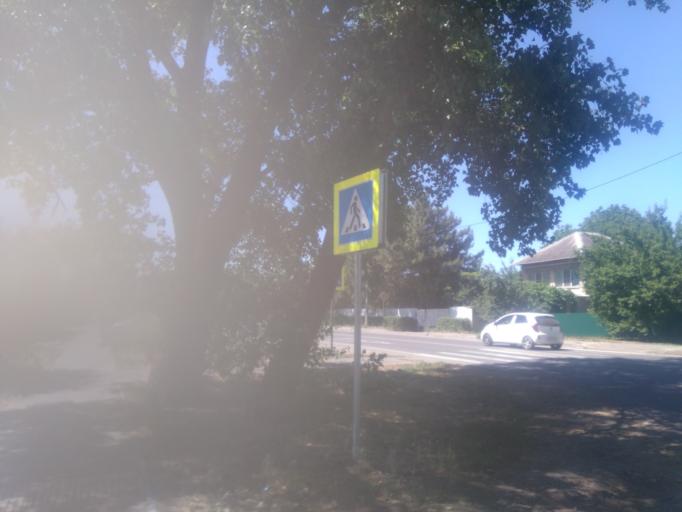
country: RU
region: Krasnodarskiy
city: Fastovetskaya
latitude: 45.9153
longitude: 40.1534
